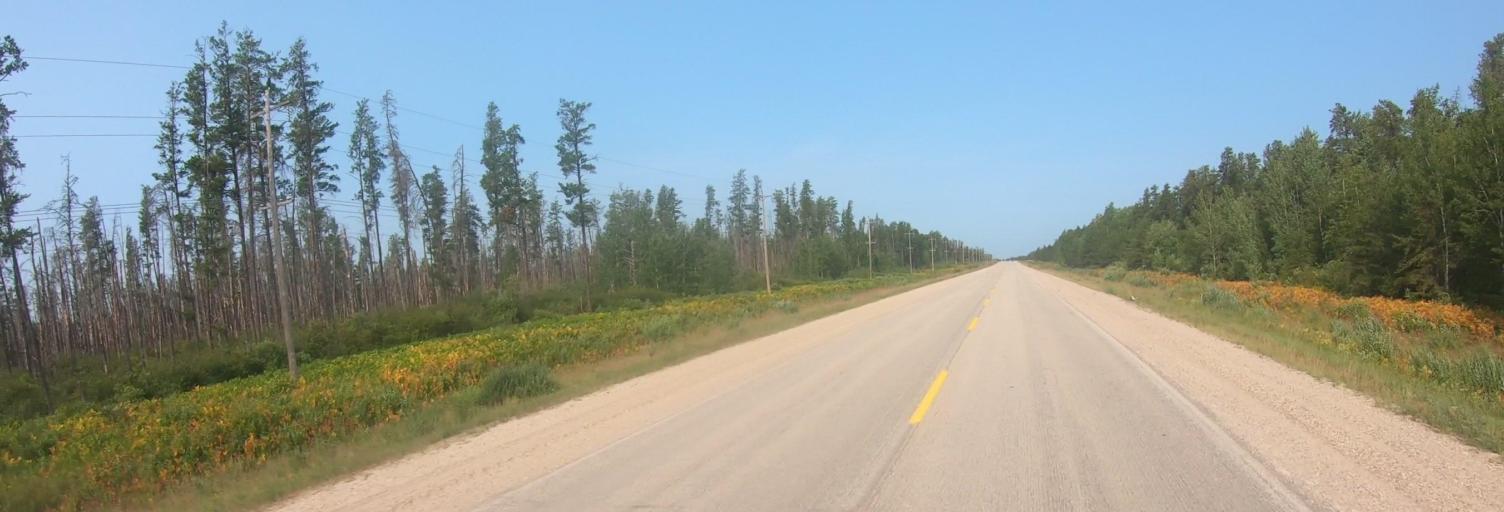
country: US
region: Minnesota
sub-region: Roseau County
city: Roseau
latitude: 49.0796
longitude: -95.8679
